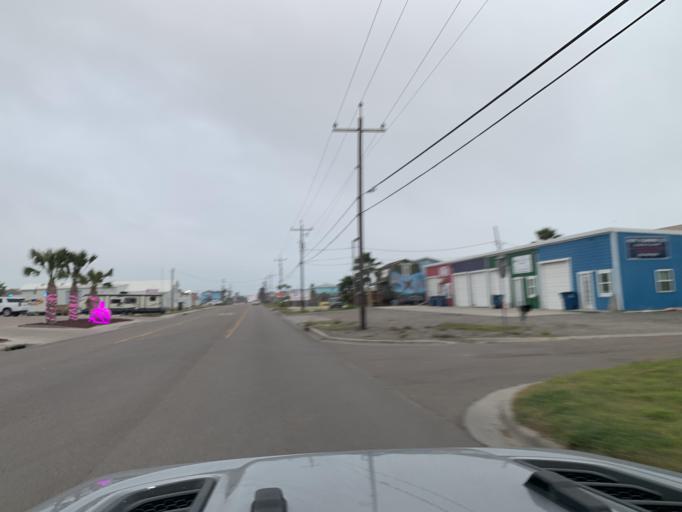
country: US
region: Texas
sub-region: Nueces County
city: Port Aransas
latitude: 27.8305
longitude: -97.0704
